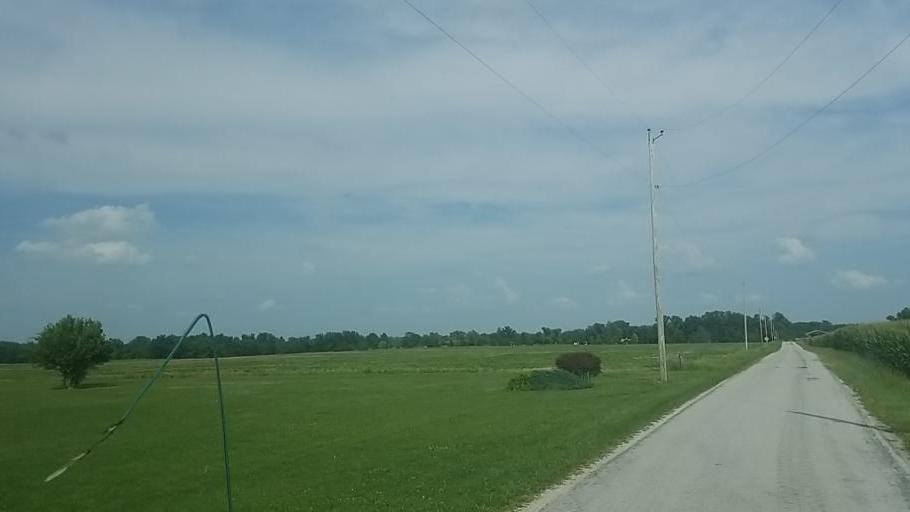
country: US
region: Ohio
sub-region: Hardin County
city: Forest
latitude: 40.7893
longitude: -83.5600
